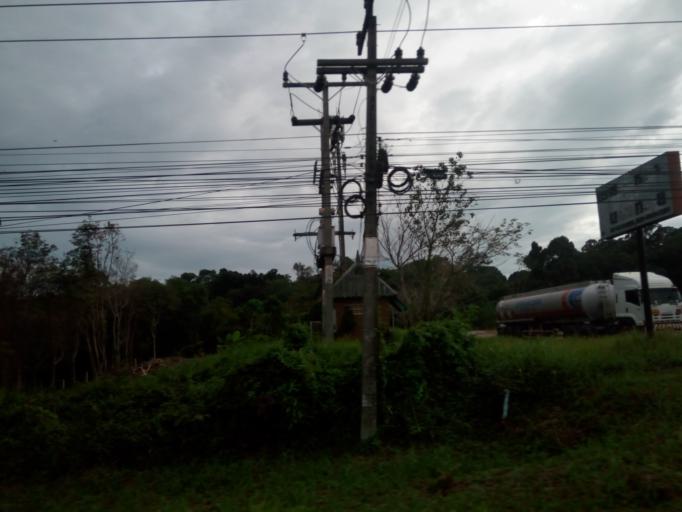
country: TH
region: Phuket
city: Thalang
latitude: 8.0904
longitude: 98.3302
